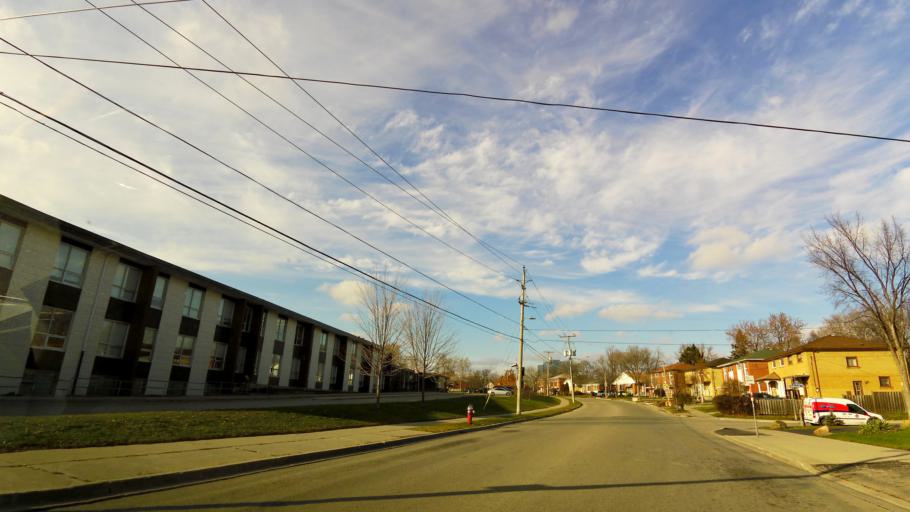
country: CA
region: Ontario
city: Mississauga
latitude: 43.5612
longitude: -79.6613
